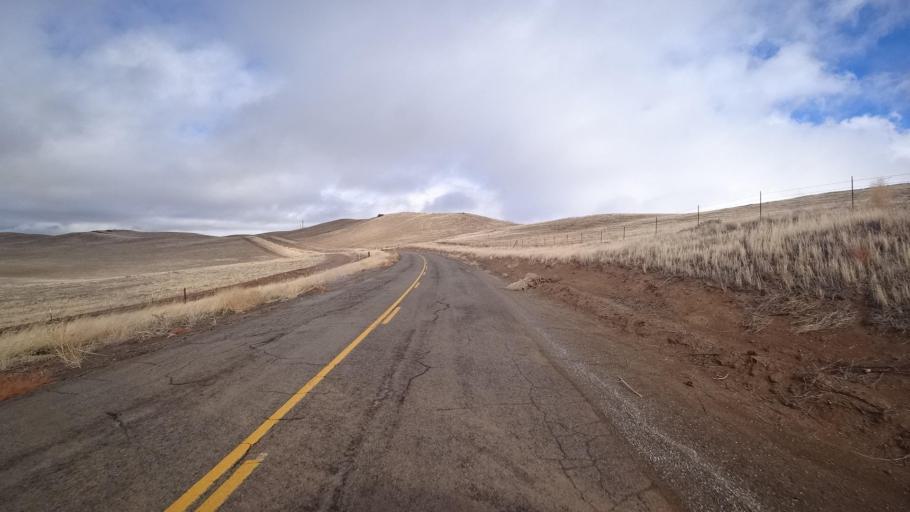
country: US
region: California
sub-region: Kern County
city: Maricopa
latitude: 34.9092
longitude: -119.3949
